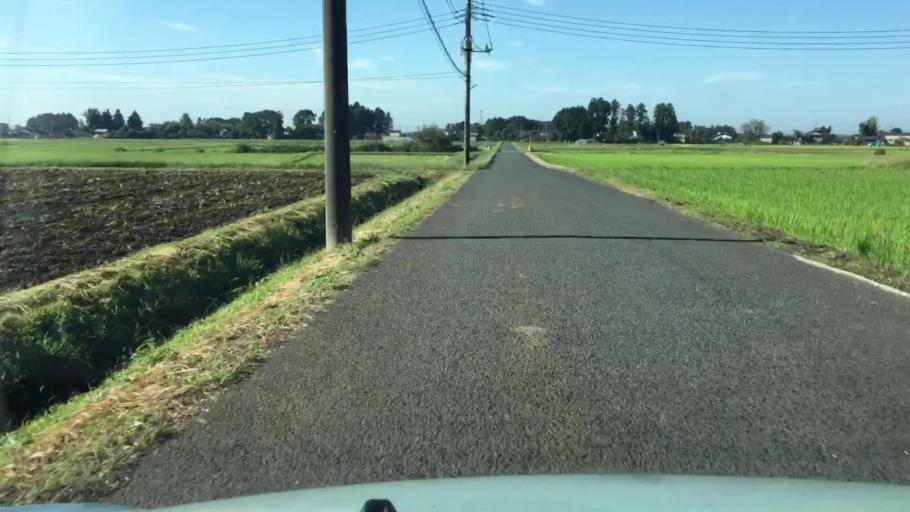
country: JP
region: Tochigi
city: Ujiie
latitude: 36.6964
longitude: 140.0120
